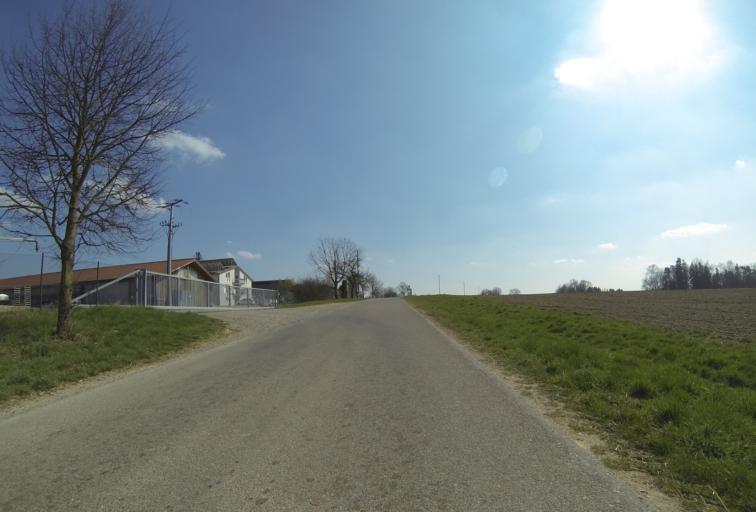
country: DE
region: Baden-Wuerttemberg
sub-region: Tuebingen Region
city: Huttisheim
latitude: 48.2877
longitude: 9.9472
